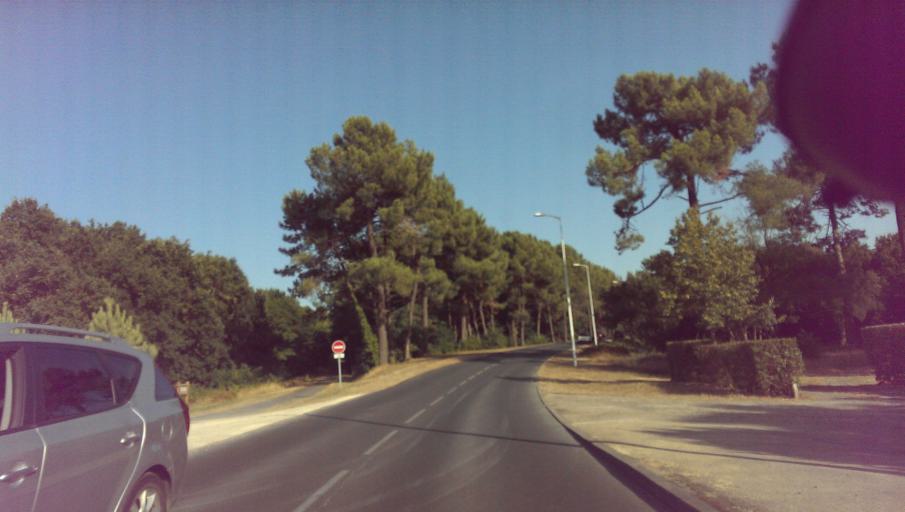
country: FR
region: Aquitaine
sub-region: Departement des Landes
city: Mimizan
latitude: 44.2066
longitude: -1.2403
